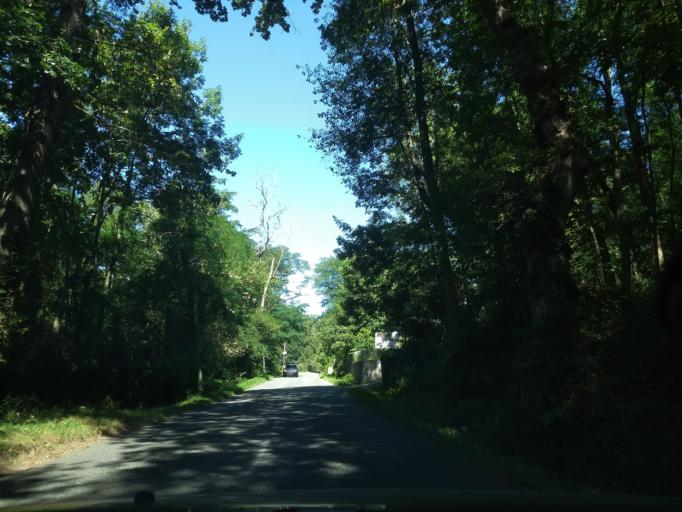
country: FR
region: Aquitaine
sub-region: Departement des Pyrenees-Atlantiques
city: Soumoulou
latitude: 43.2716
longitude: -0.1860
